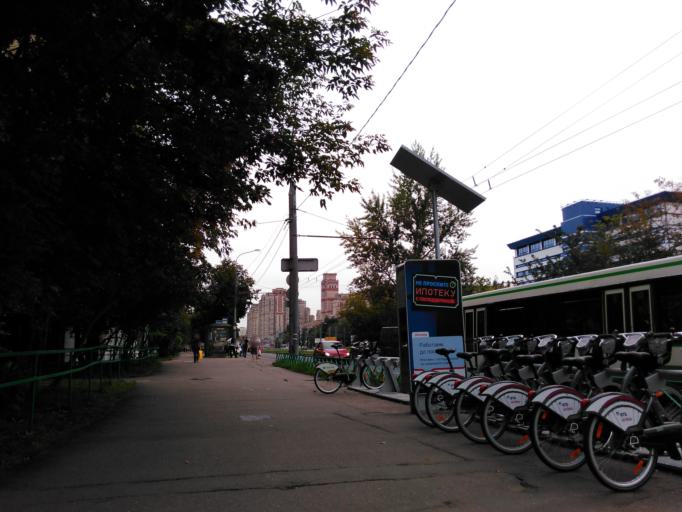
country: RU
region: Moskovskaya
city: Kastanayevo
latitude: 55.7104
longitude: 37.5072
